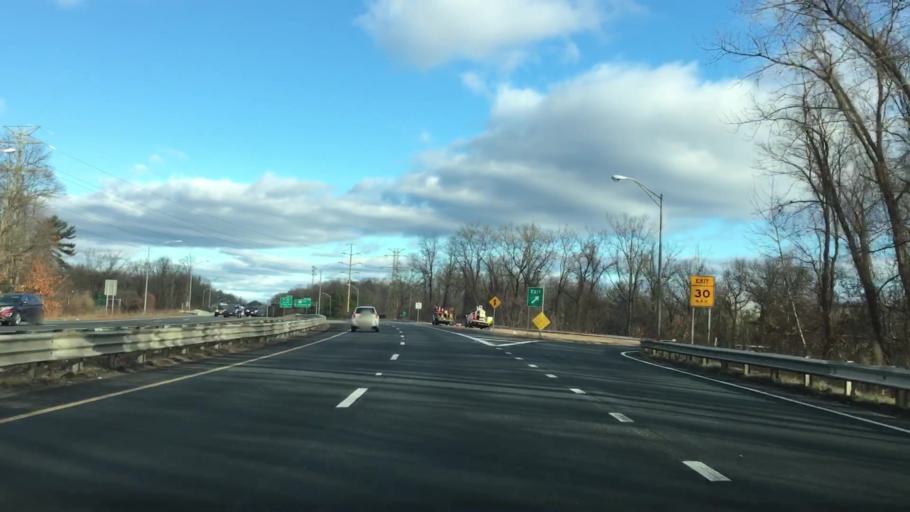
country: US
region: Massachusetts
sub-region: Hampden County
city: Springfield
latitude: 42.1436
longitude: -72.5495
